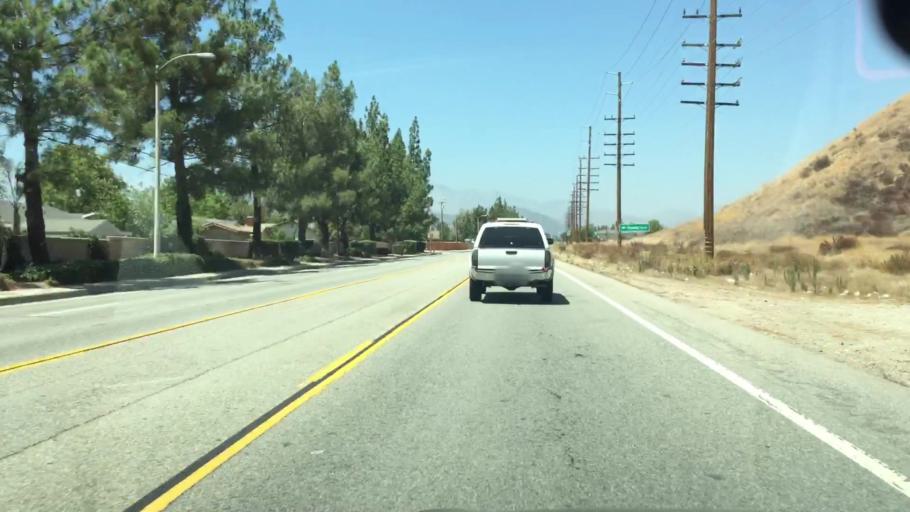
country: US
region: California
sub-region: San Bernardino County
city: Muscoy
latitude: 34.1776
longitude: -117.3340
